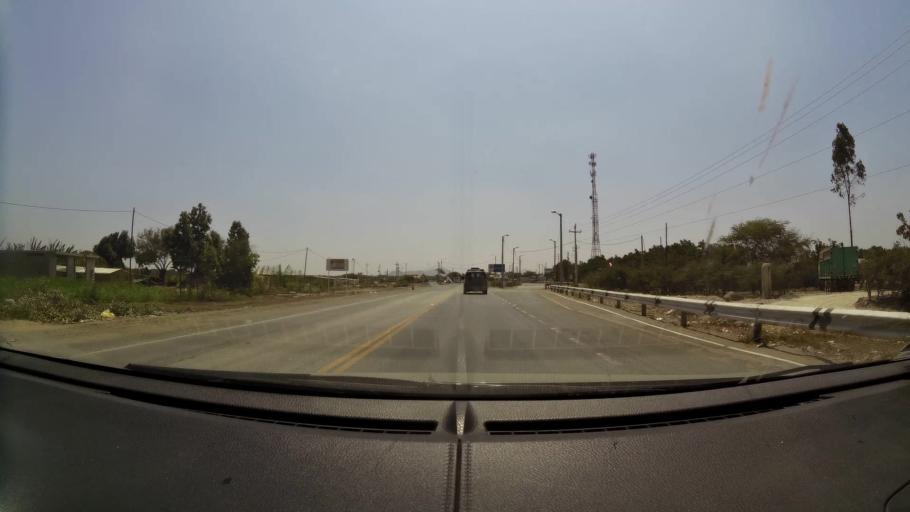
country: PE
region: Lambayeque
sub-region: Provincia de Chiclayo
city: Mocupe
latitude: -7.0217
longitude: -79.6018
